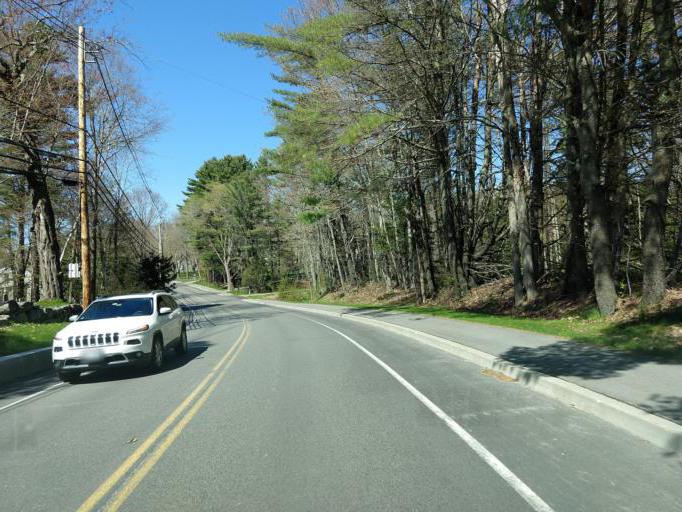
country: US
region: Maine
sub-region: York County
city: Kennebunkport
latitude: 43.3691
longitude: -70.4732
